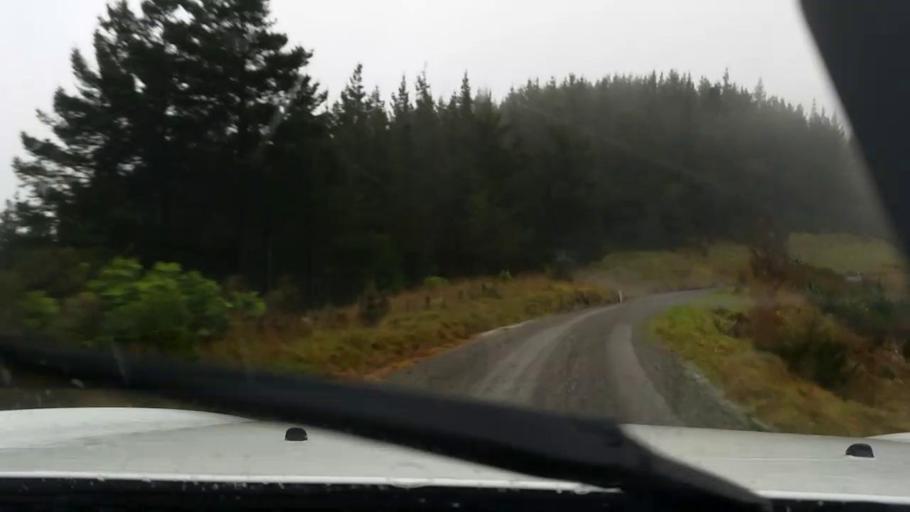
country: NZ
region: Wellington
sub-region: Masterton District
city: Masterton
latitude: -41.1889
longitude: 175.8176
